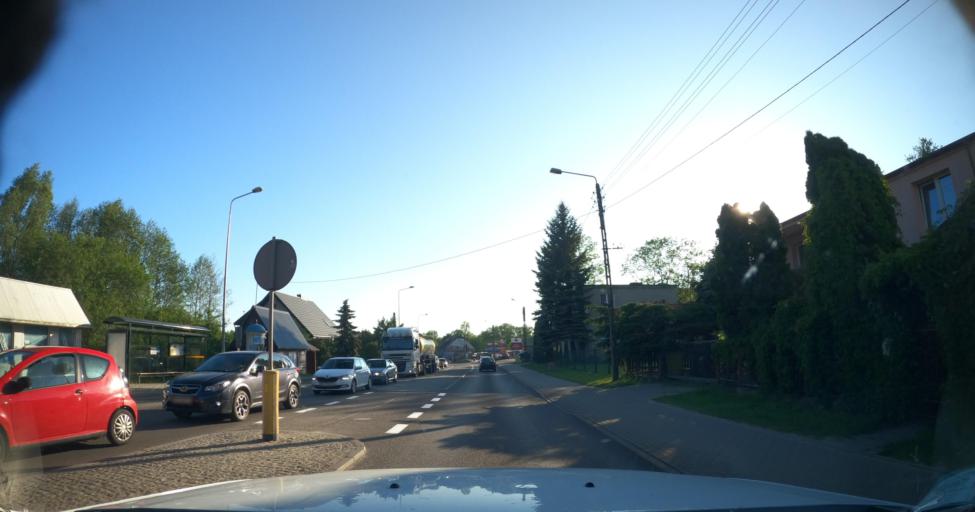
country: PL
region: Pomeranian Voivodeship
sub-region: Powiat kartuski
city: Zukowo
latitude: 54.3423
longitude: 18.3579
